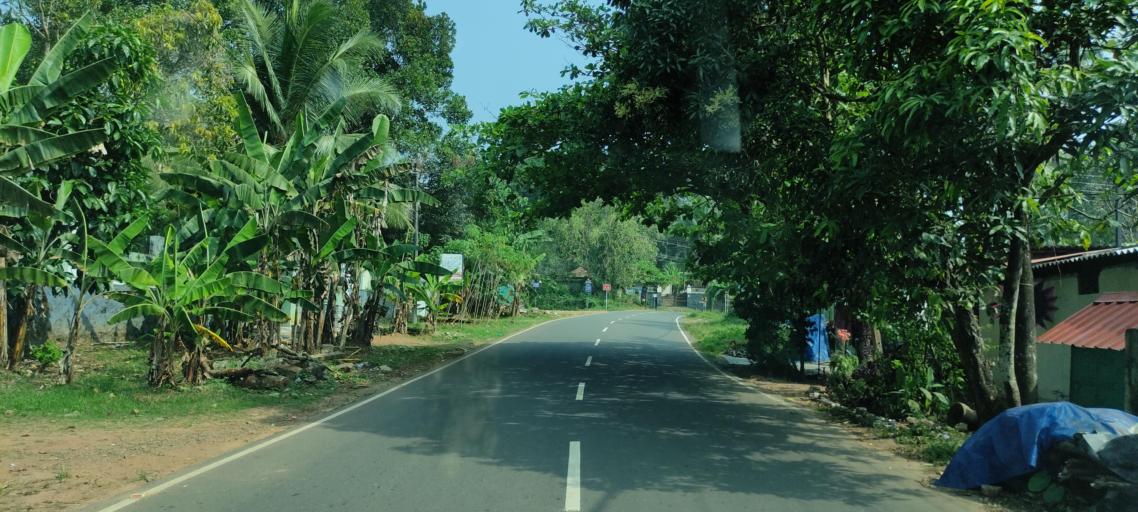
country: IN
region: Kerala
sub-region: Alappuzha
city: Chengannur
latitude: 9.2441
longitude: 76.6749
